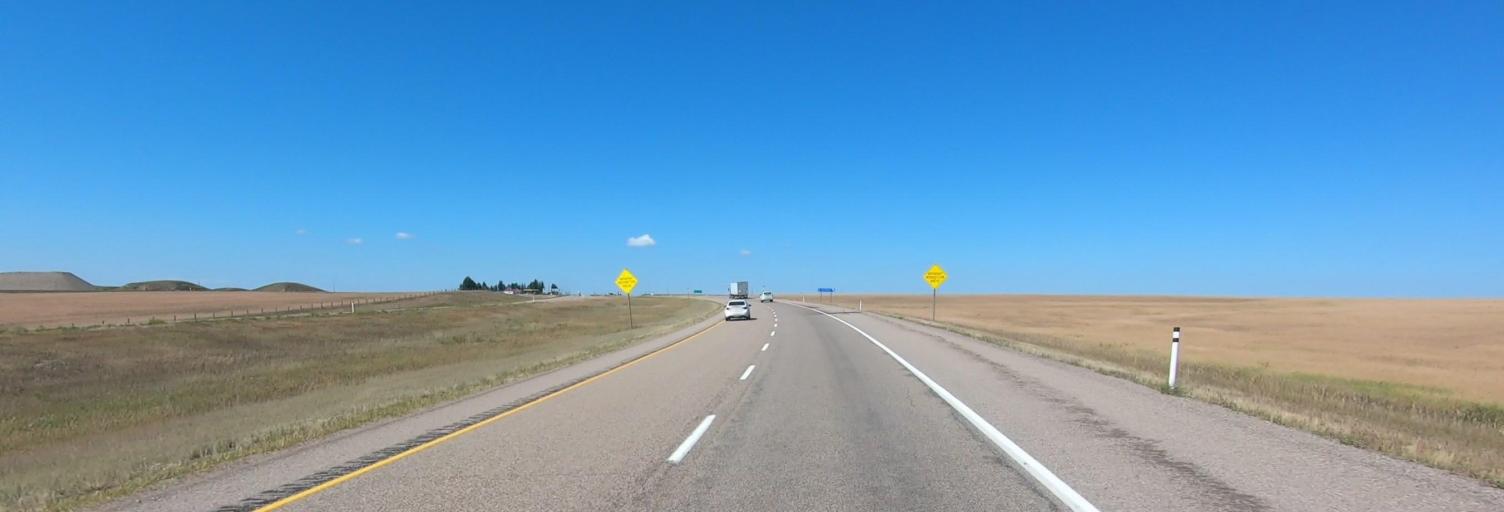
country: CA
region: Alberta
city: Bassano
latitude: 50.8634
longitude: -112.8563
